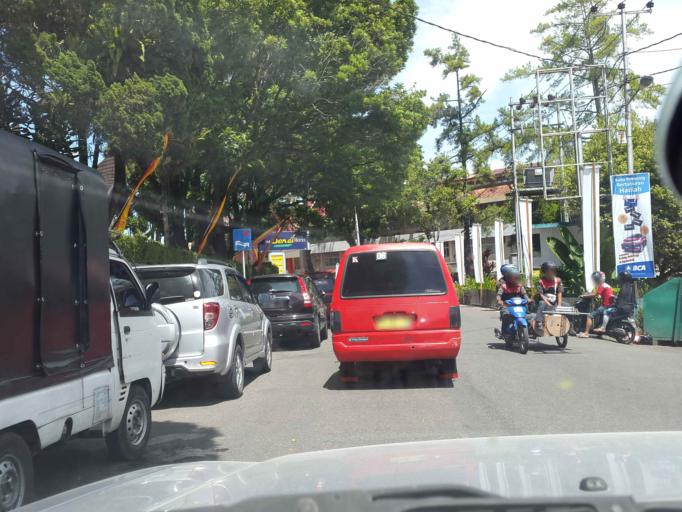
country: ID
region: West Sumatra
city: Bukittinggi
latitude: -0.2992
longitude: 100.3676
